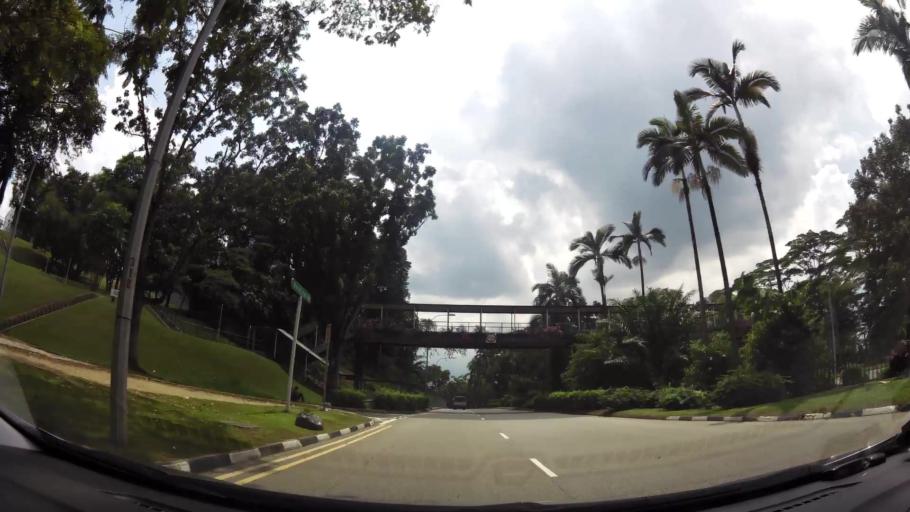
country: MY
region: Johor
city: Johor Bahru
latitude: 1.4300
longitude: 103.7619
